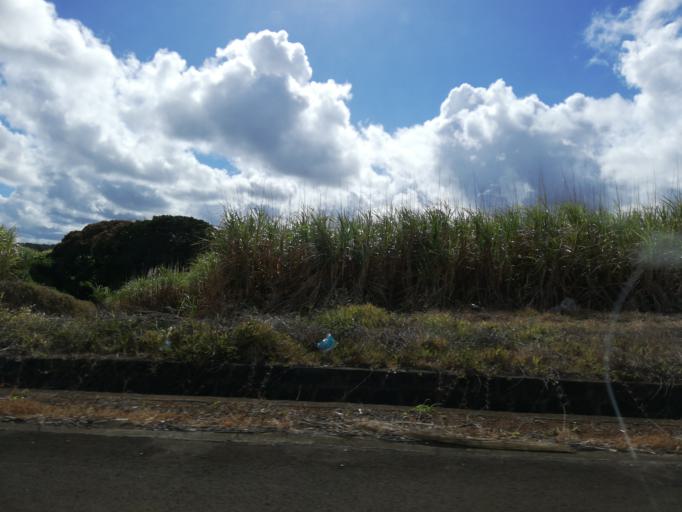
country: MU
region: Grand Port
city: Mahebourg
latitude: -20.4034
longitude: 57.6772
